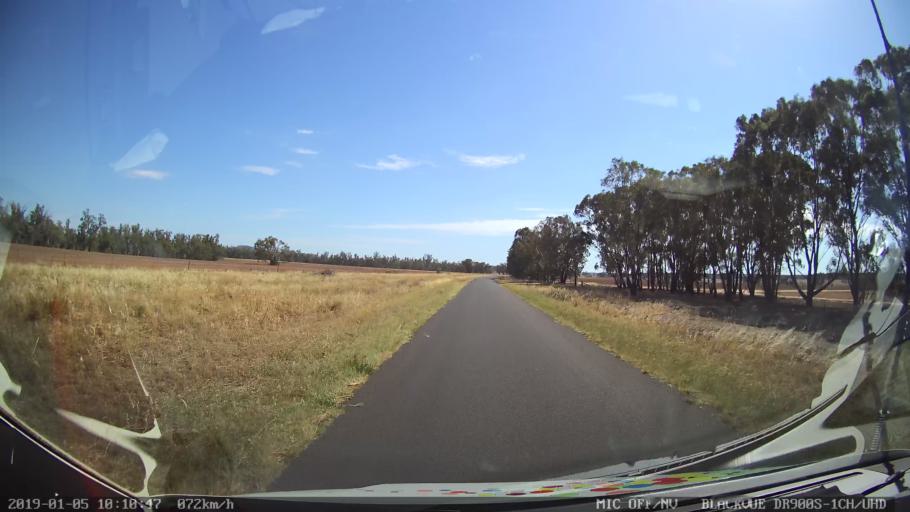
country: AU
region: New South Wales
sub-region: Gilgandra
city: Gilgandra
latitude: -31.6185
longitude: 148.8954
